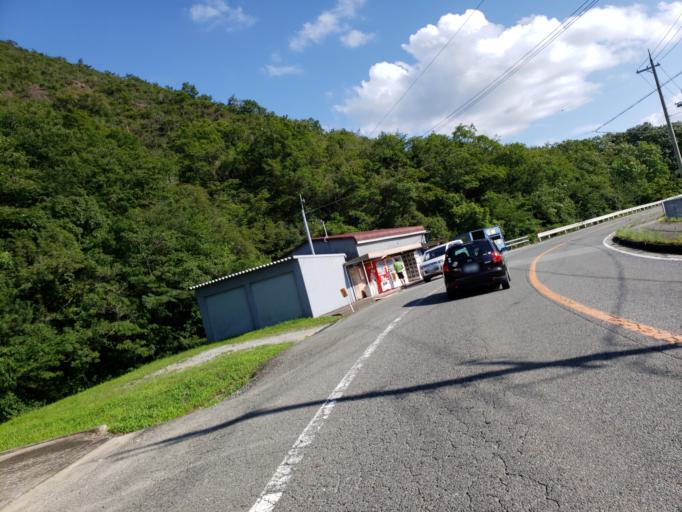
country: JP
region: Hyogo
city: Kakogawacho-honmachi
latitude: 34.8797
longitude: 134.7997
